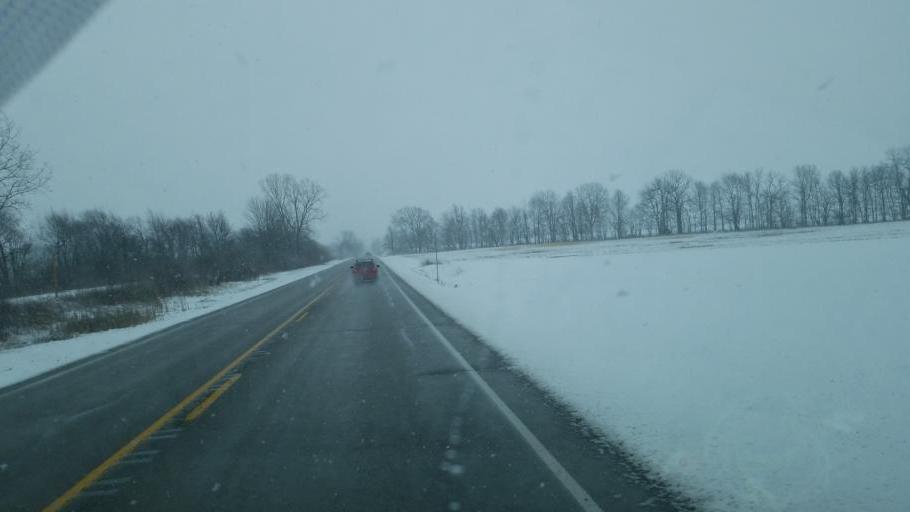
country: US
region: Indiana
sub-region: Randolph County
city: Parker City
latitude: 40.0464
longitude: -85.2175
